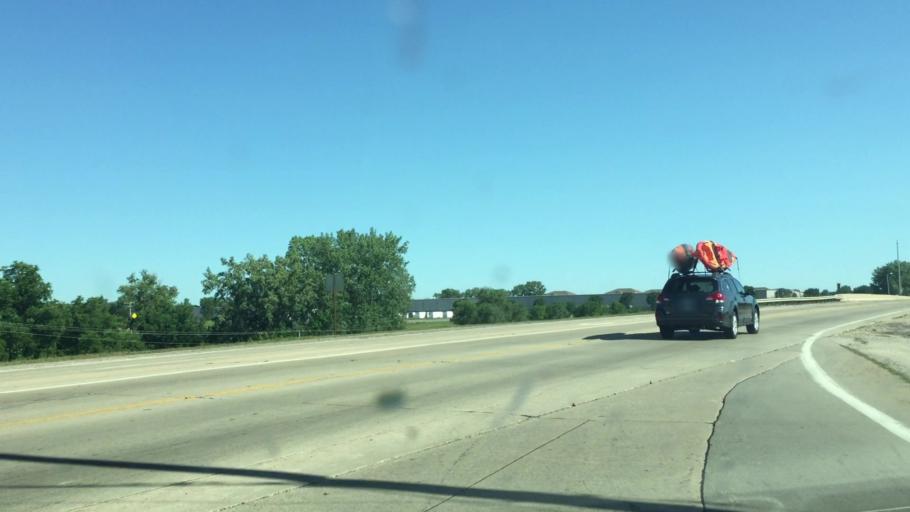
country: US
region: Iowa
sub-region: Linn County
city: Ely
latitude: 41.9282
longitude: -91.6376
